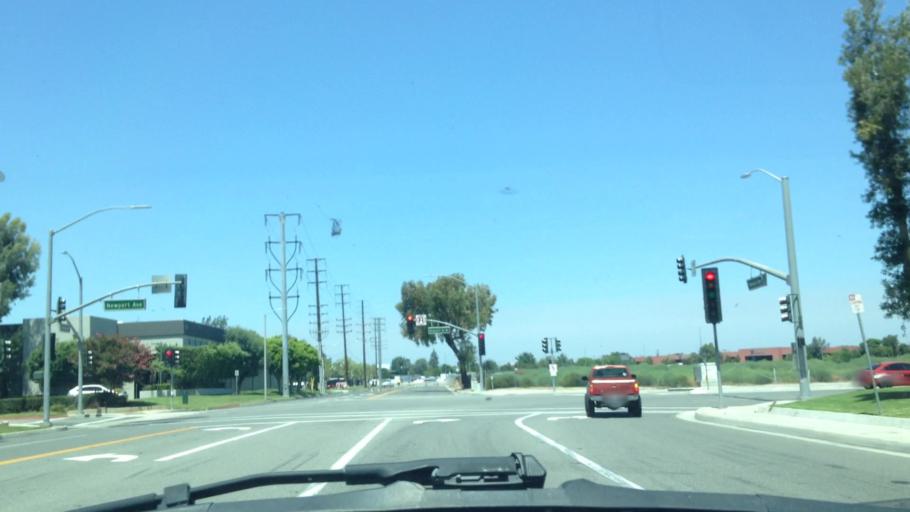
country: US
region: California
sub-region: Orange County
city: Tustin
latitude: 33.7196
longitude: -117.8360
